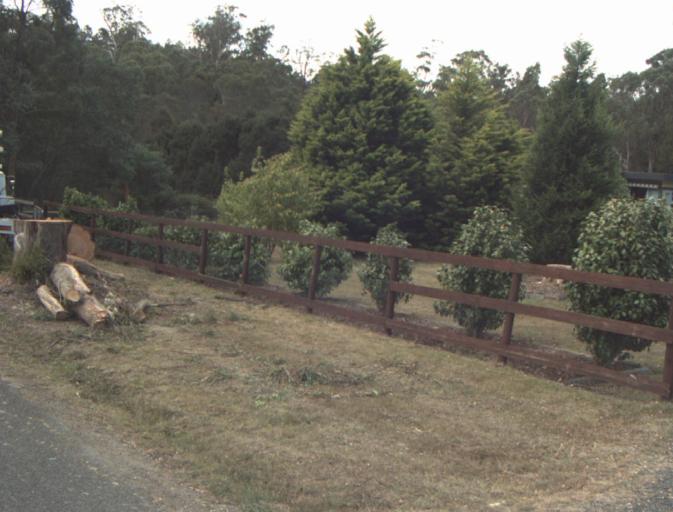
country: AU
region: Tasmania
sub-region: Launceston
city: Mayfield
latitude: -41.3023
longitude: 147.0349
